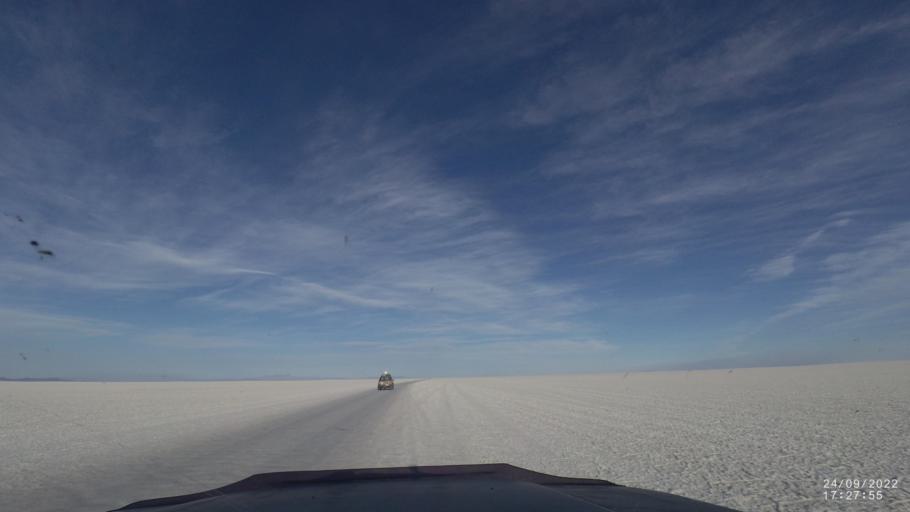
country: BO
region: Potosi
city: Colchani
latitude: -20.3014
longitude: -67.4383
